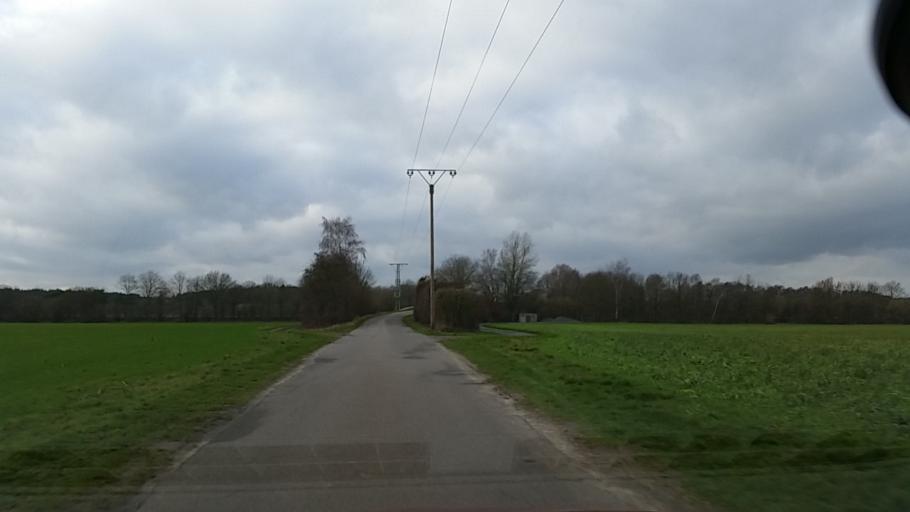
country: DE
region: Lower Saxony
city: Luder
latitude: 52.7642
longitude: 10.6747
